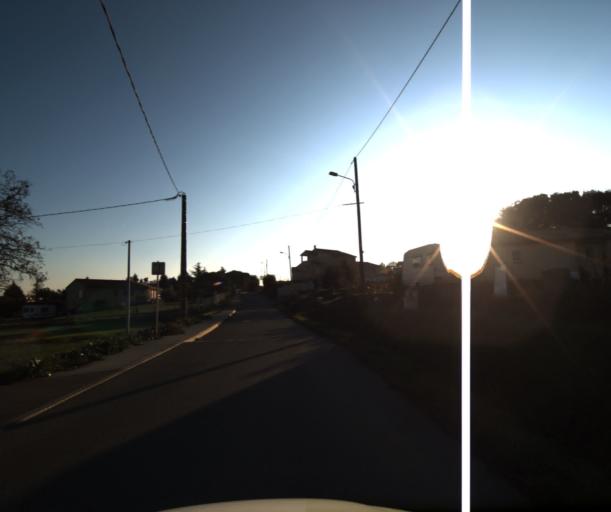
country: FR
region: Midi-Pyrenees
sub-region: Departement de la Haute-Garonne
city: Colomiers
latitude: 43.6217
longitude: 1.3412
